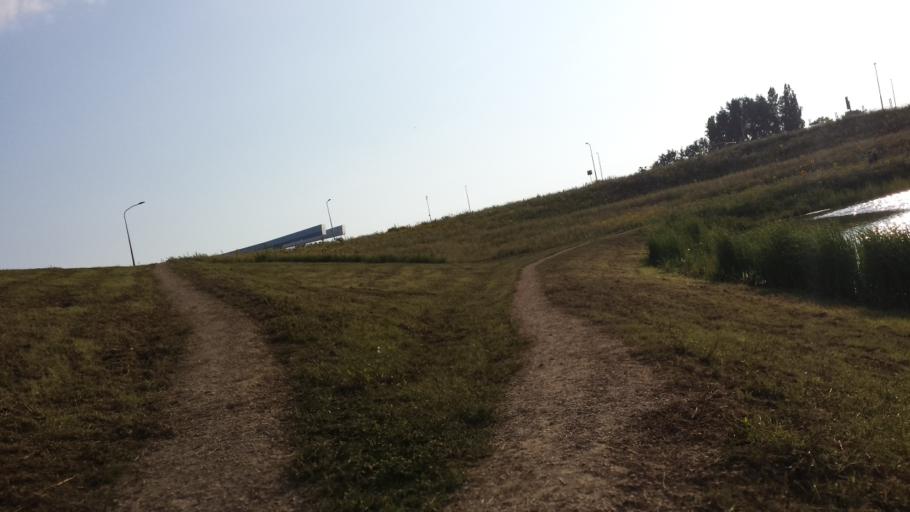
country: NL
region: South Holland
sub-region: Gemeente Gouda
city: Gouda
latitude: 51.9980
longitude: 4.6979
